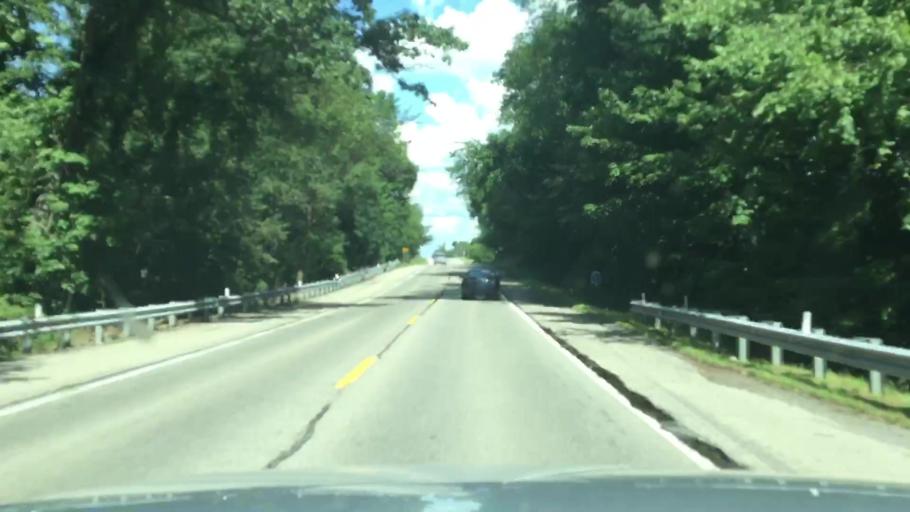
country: US
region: Michigan
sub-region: Lenawee County
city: Clinton
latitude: 42.1138
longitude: -83.8834
